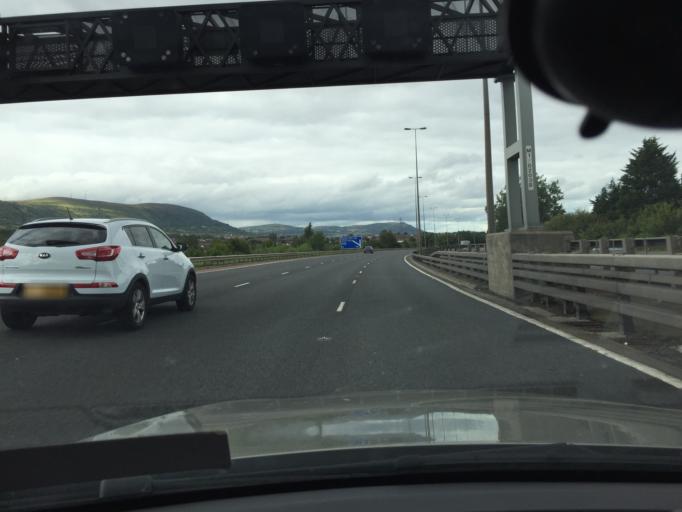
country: GB
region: Northern Ireland
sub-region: Lisburn District
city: Lisburn
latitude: 54.5649
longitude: -5.9929
